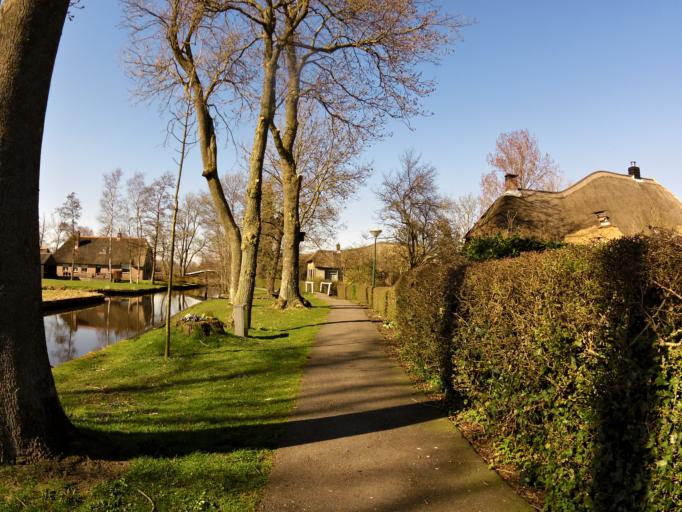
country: NL
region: Overijssel
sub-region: Gemeente Steenwijkerland
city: Giethoorn
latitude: 52.7500
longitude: 6.0841
